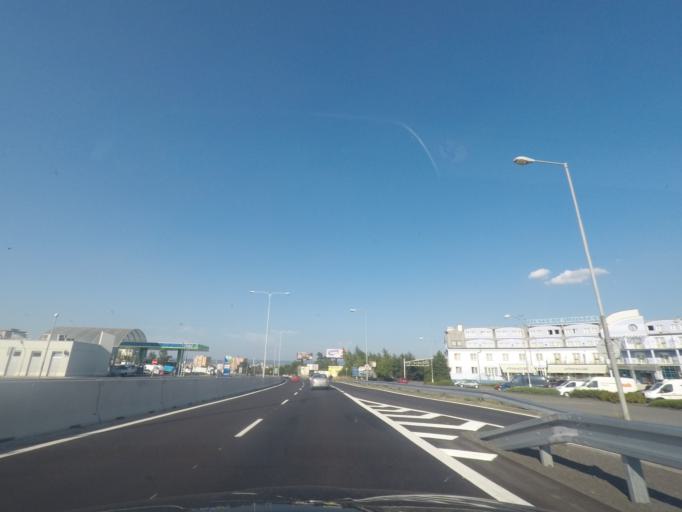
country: CZ
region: Olomoucky
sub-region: Okres Olomouc
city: Olomouc
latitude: 49.5726
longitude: 17.2317
